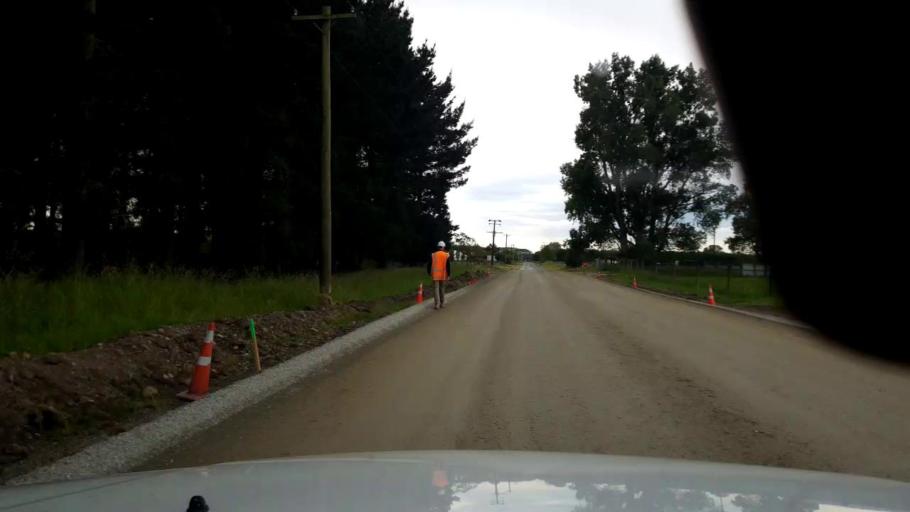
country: NZ
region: Canterbury
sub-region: Timaru District
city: Pleasant Point
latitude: -44.2756
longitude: 171.2517
